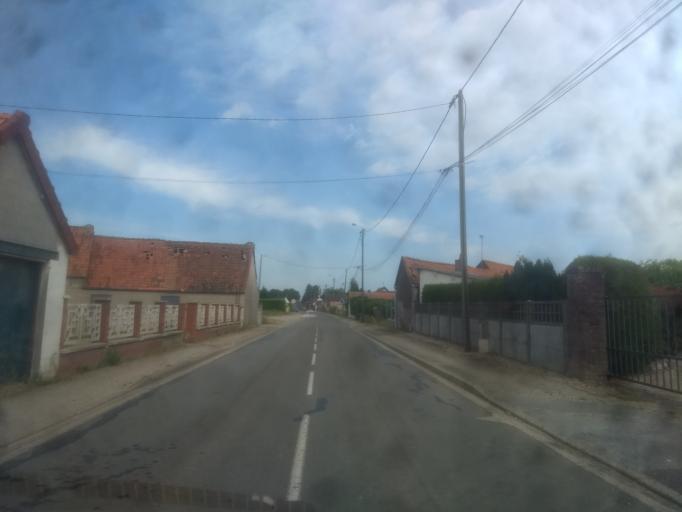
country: FR
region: Picardie
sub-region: Departement de la Somme
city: Nouvion
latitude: 50.1857
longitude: 1.8343
